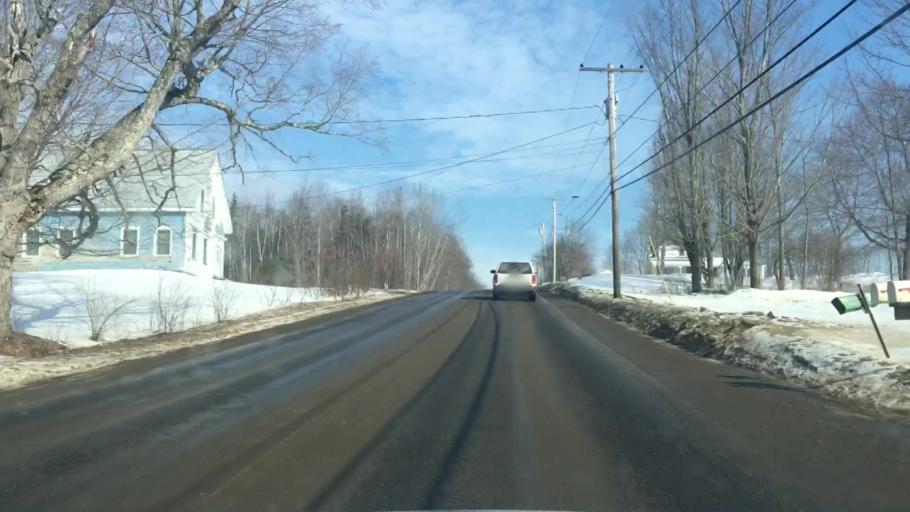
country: US
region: Maine
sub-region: Penobscot County
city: Hermon
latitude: 44.8324
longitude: -68.8803
